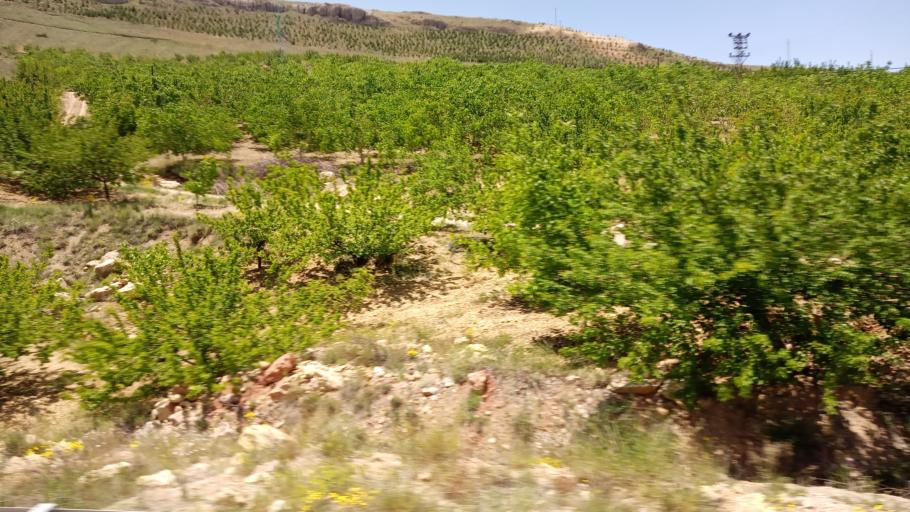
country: TR
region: Malatya
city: Darende
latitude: 38.6150
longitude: 37.4570
